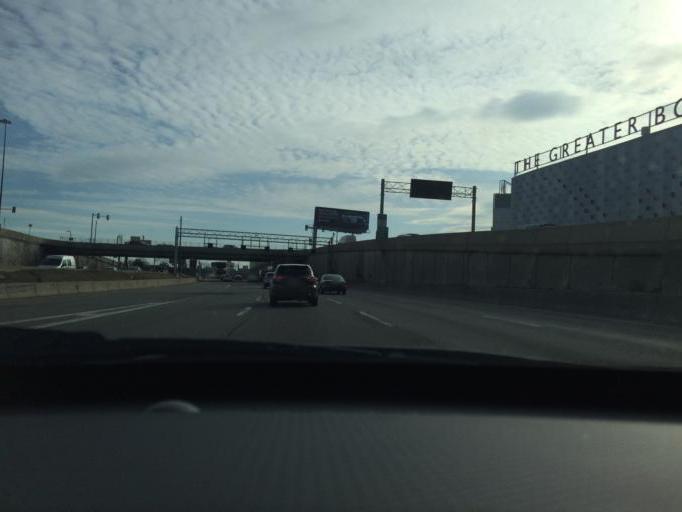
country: US
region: Massachusetts
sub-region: Suffolk County
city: South Boston
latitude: 42.3351
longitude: -71.0653
